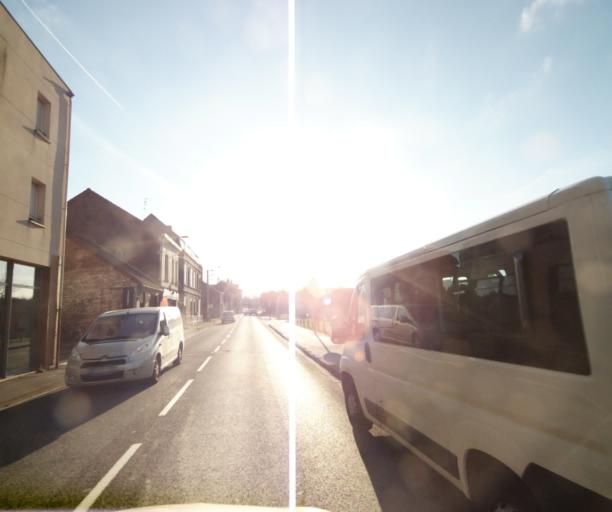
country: FR
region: Nord-Pas-de-Calais
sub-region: Departement du Nord
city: Valenciennes
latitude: 50.3478
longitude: 3.5344
